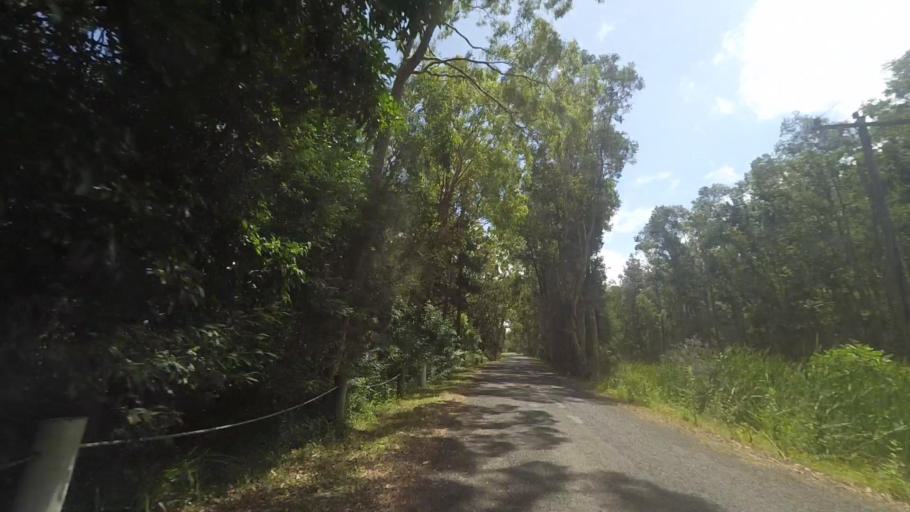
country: AU
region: New South Wales
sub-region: Great Lakes
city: Bulahdelah
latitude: -32.5085
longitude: 152.2990
